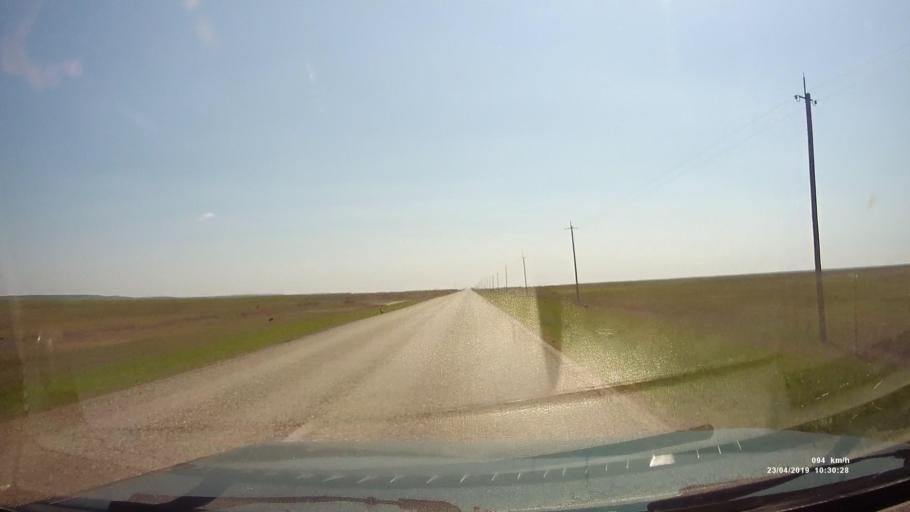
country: RU
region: Kalmykiya
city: Yashalta
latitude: 46.5919
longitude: 42.5450
